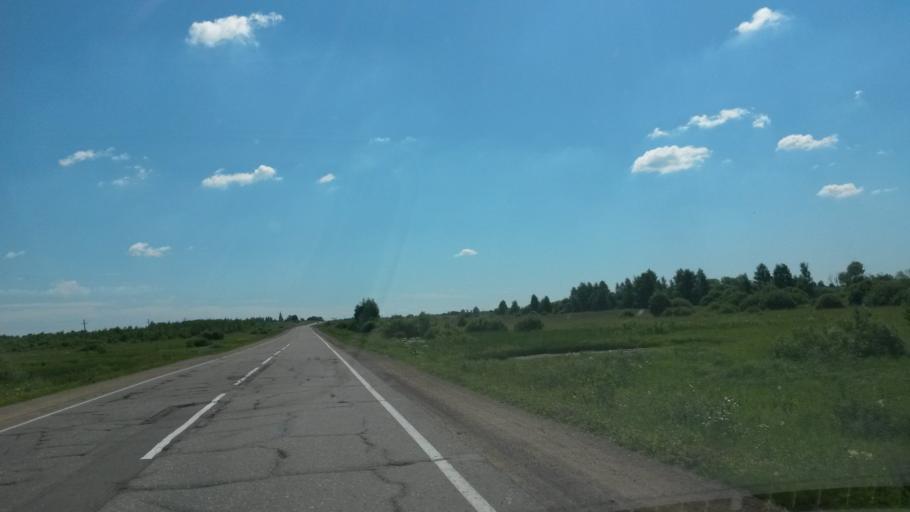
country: RU
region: Jaroslavl
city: Dubki
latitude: 57.2403
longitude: 40.1696
